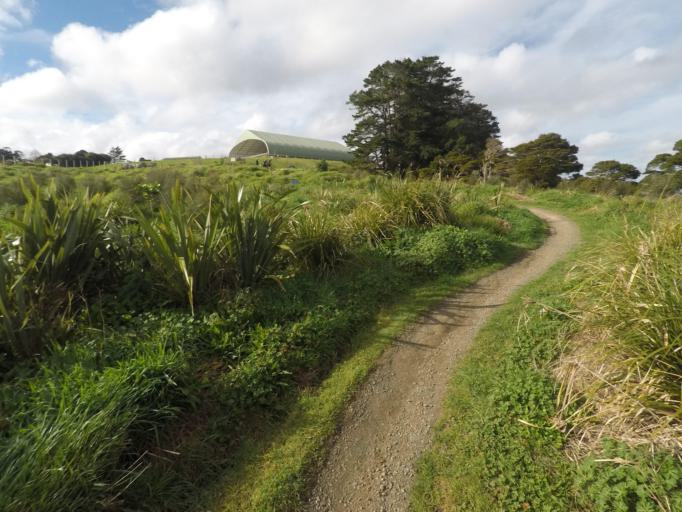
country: NZ
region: Auckland
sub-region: Auckland
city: Manukau City
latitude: -36.9955
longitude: 174.9133
